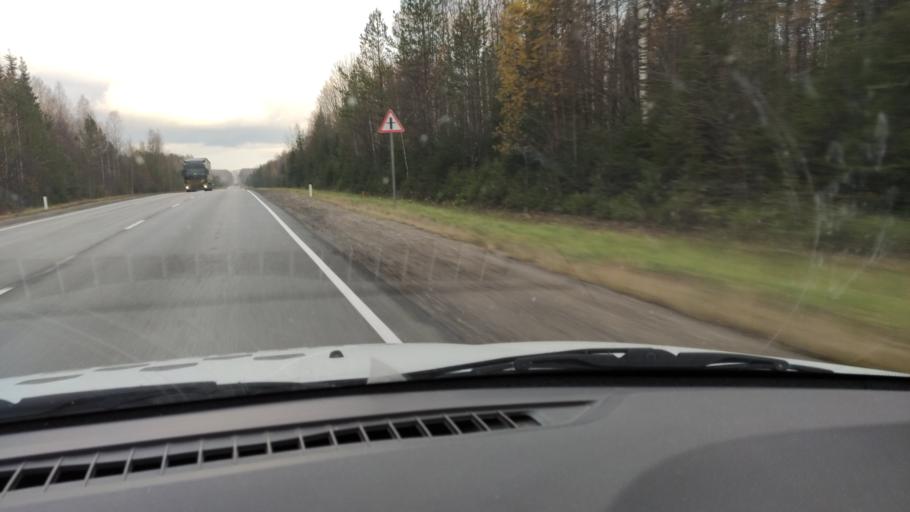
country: RU
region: Kirov
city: Chernaya Kholunitsa
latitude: 58.8130
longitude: 51.8294
